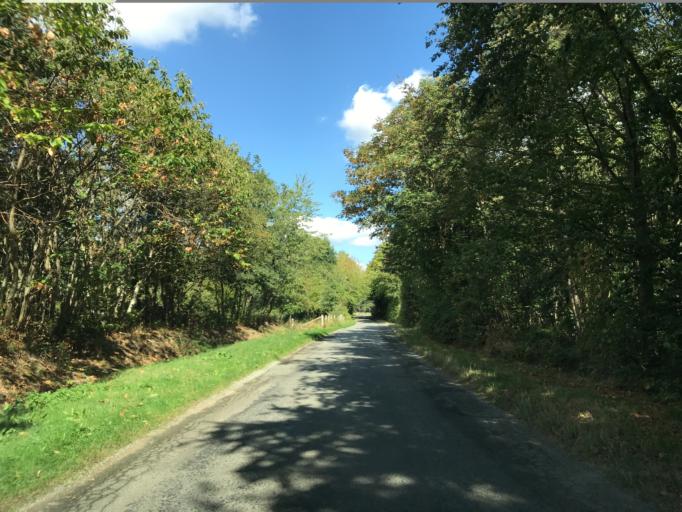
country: FR
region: Haute-Normandie
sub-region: Departement de l'Eure
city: La Chapelle-Reanville
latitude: 49.0972
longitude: 1.3905
